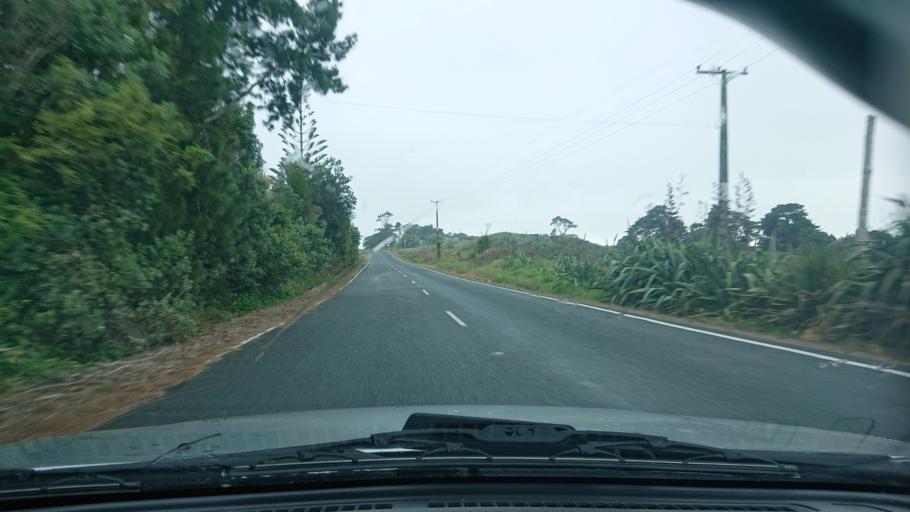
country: NZ
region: Auckland
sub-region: Auckland
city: Wellsford
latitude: -36.3297
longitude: 174.4062
